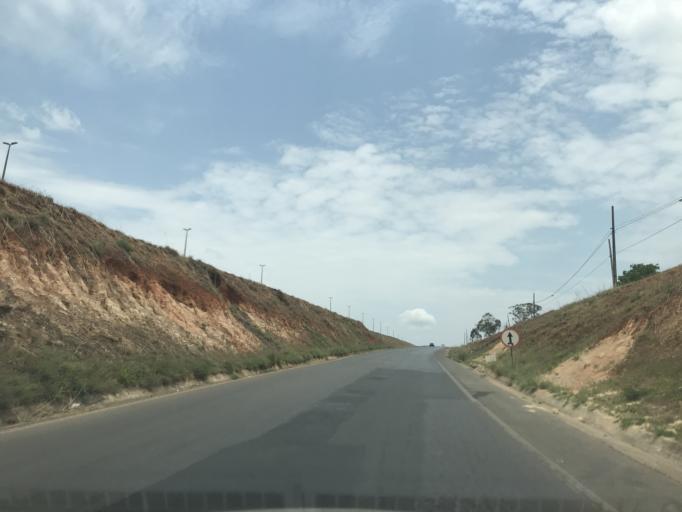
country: BR
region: Federal District
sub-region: Brasilia
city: Brasilia
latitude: -15.6706
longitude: -47.8170
